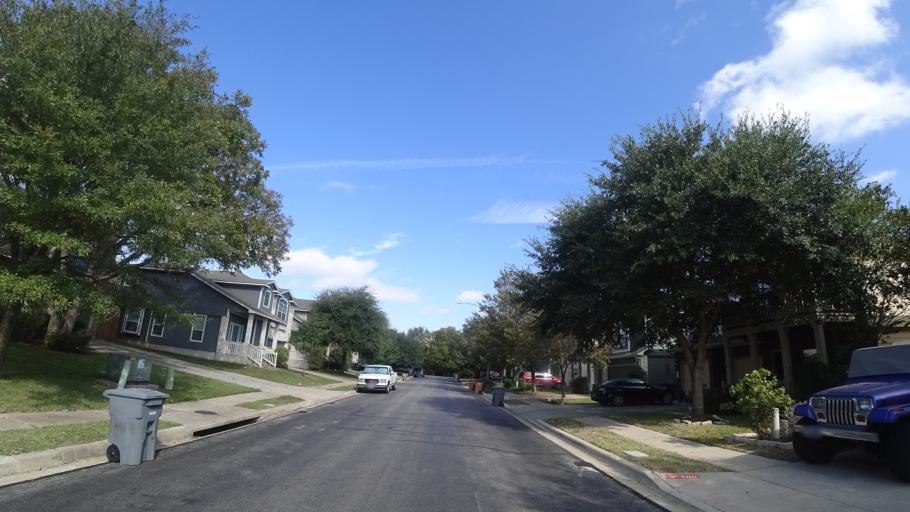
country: US
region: Texas
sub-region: Travis County
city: Shady Hollow
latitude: 30.1906
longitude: -97.8170
